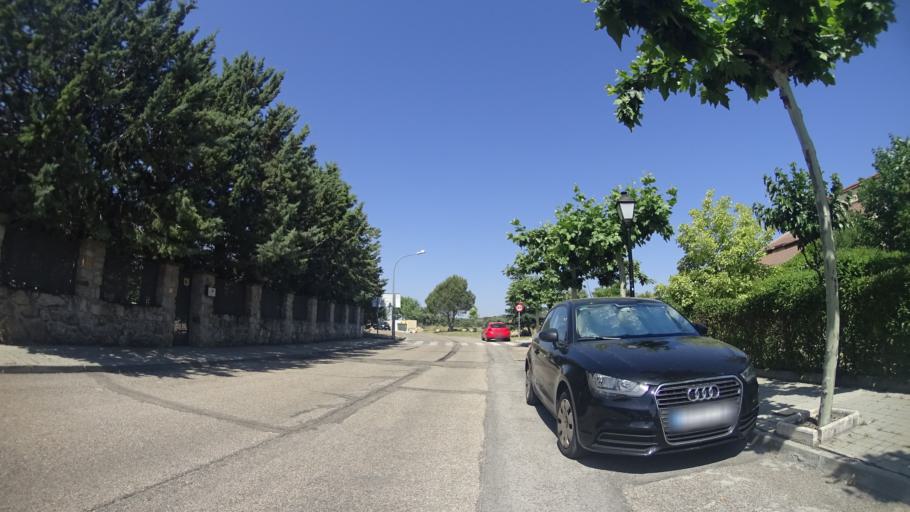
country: ES
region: Madrid
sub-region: Provincia de Madrid
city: Hoyo de Manzanares
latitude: 40.6072
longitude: -3.9001
